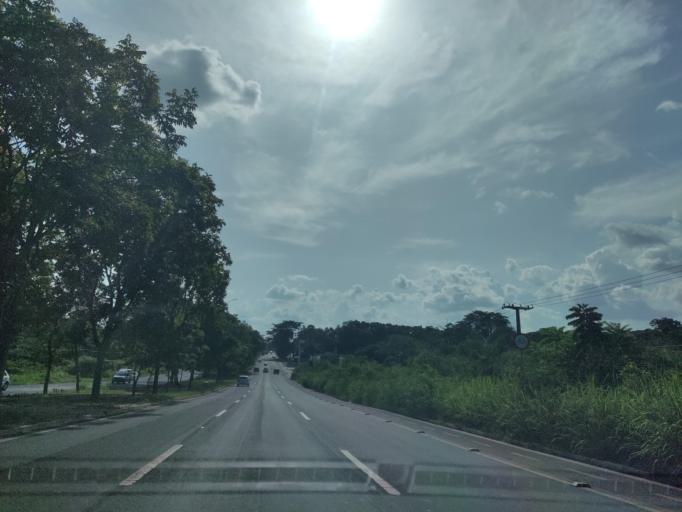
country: BR
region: Piaui
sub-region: Teresina
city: Teresina
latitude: -5.0795
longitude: -42.7553
